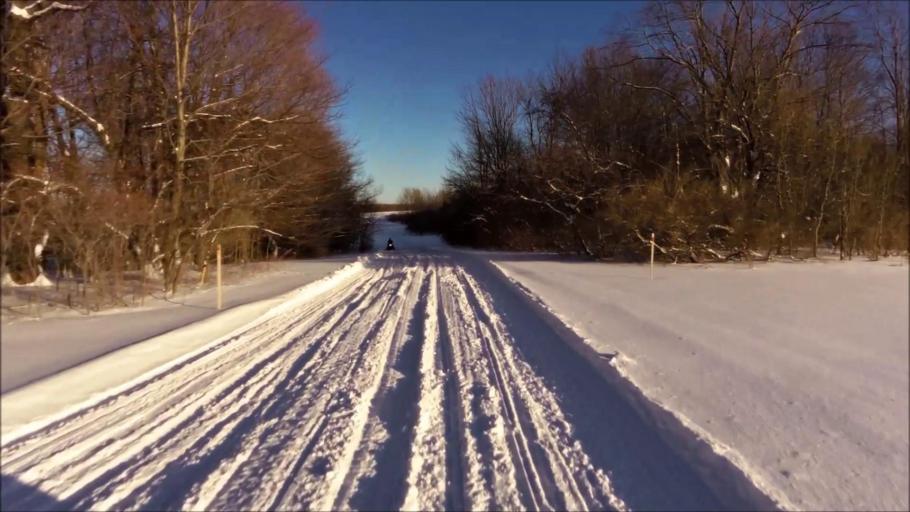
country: US
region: New York
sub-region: Chautauqua County
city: Lakewood
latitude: 42.2263
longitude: -79.3424
